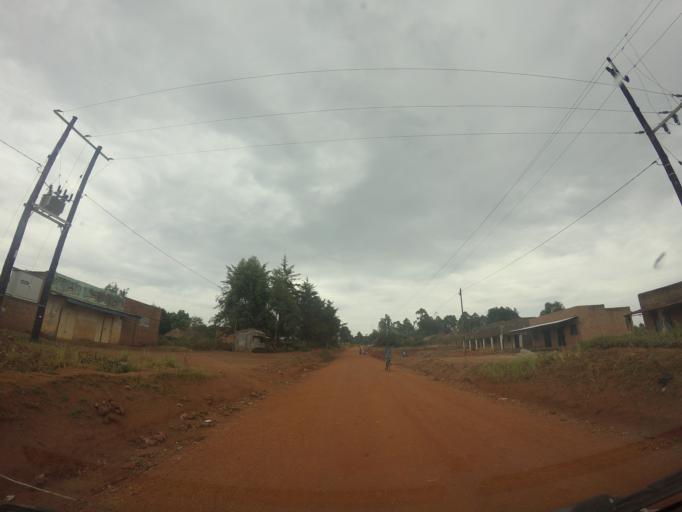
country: UG
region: Northern Region
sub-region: Zombo District
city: Zombo
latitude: 2.7569
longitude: 30.8521
